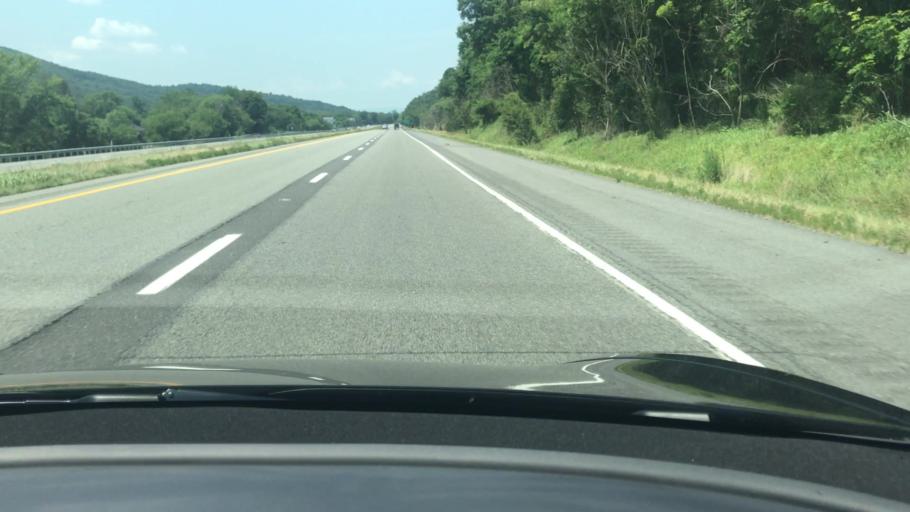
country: US
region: Pennsylvania
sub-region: Perry County
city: Newport
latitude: 40.5656
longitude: -77.1775
